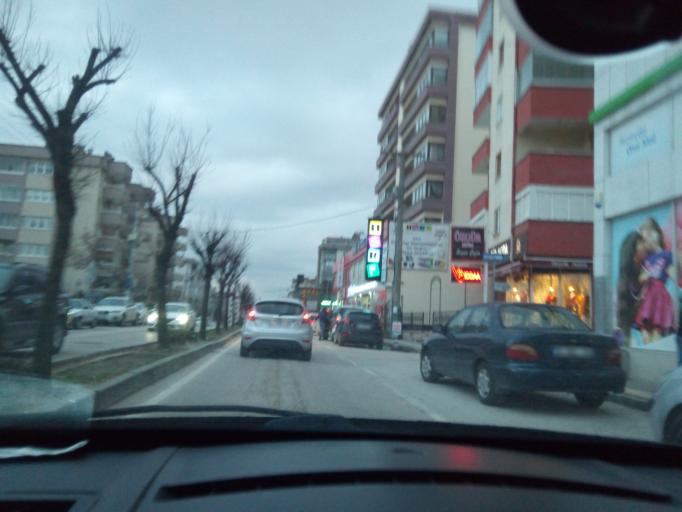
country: TR
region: Bursa
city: Yildirim
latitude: 40.2244
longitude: 28.9815
